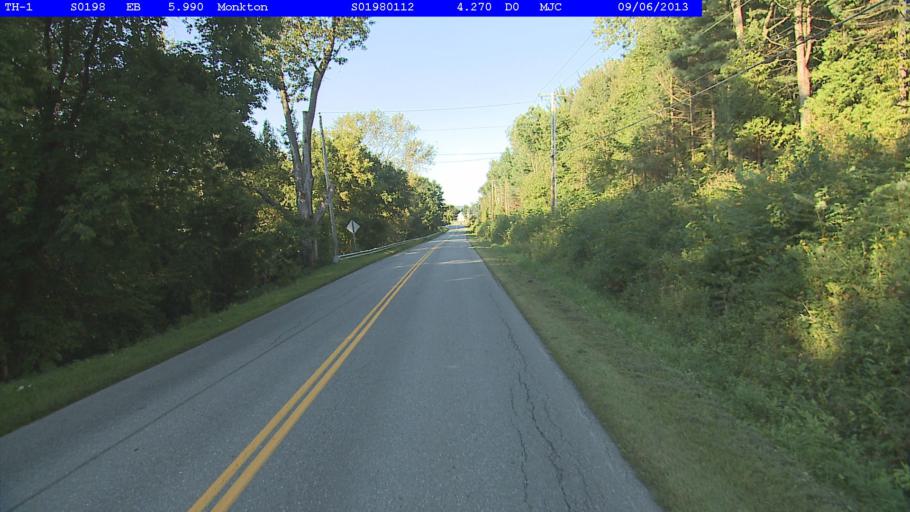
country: US
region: Vermont
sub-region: Chittenden County
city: Hinesburg
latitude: 44.2495
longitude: -73.1280
